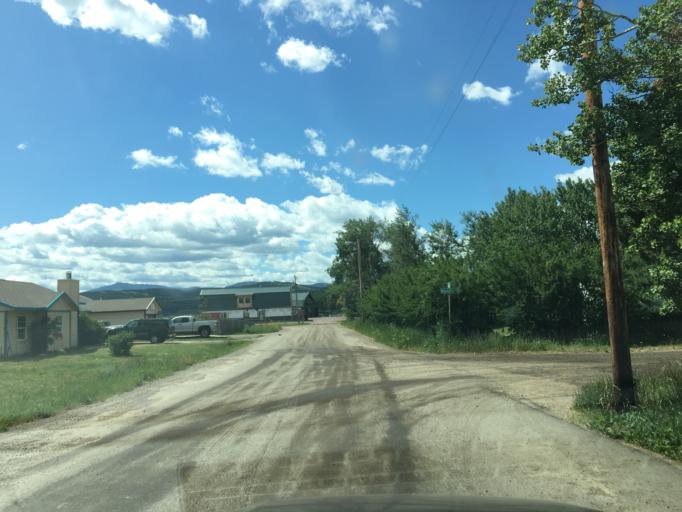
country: US
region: Montana
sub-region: Glacier County
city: South Browning
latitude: 48.4411
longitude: -113.2146
